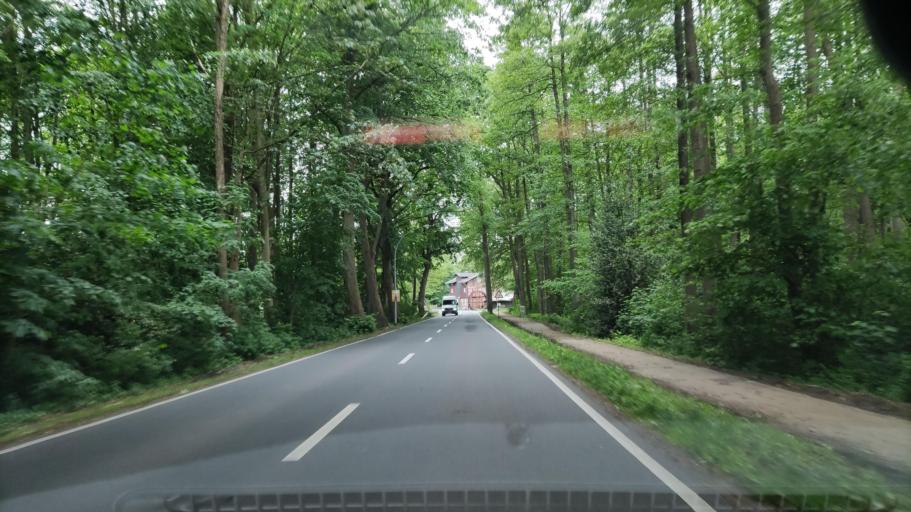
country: DE
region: Lower Saxony
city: Fintel
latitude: 53.1107
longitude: 9.6904
